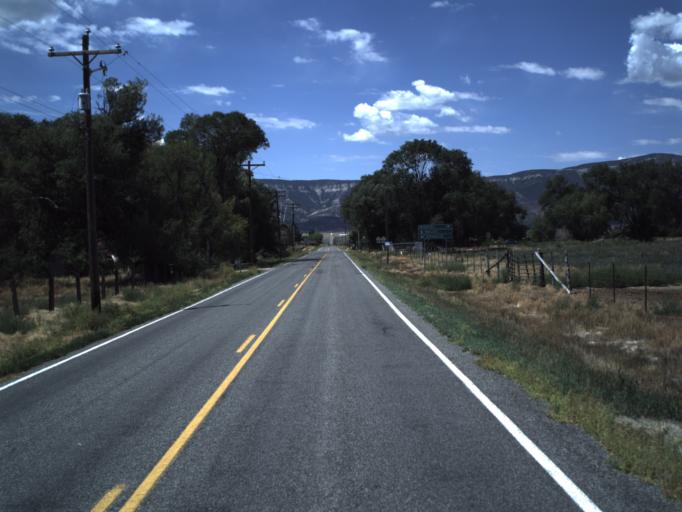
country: US
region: Utah
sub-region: Sanpete County
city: Moroni
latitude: 39.4762
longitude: -111.5603
